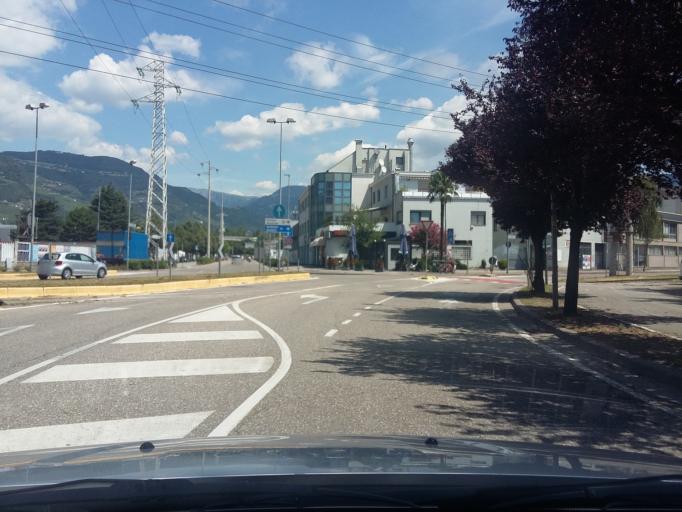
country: IT
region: Trentino-Alto Adige
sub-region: Bolzano
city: Bolzano
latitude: 46.4824
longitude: 11.3310
